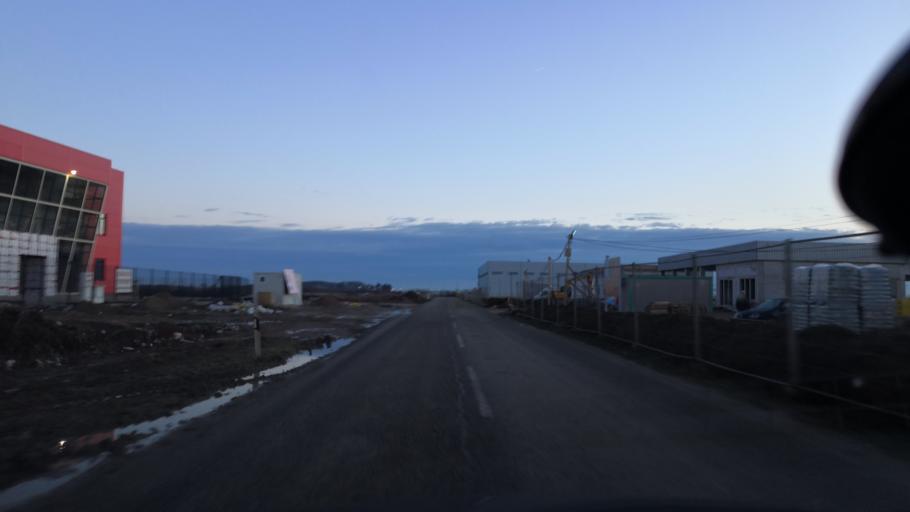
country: RS
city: Simanovci
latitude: 44.8866
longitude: 20.1121
